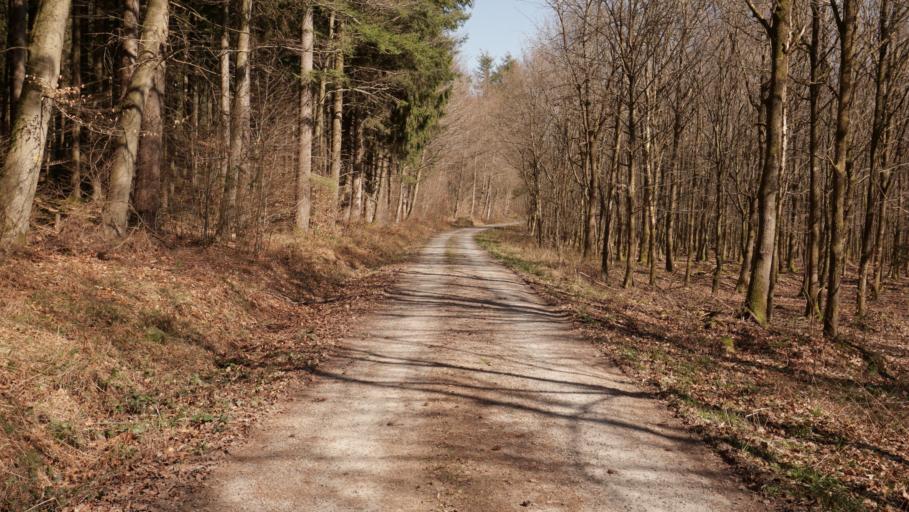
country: DE
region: Baden-Wuerttemberg
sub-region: Karlsruhe Region
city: Fahrenbach
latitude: 49.4419
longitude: 9.1450
